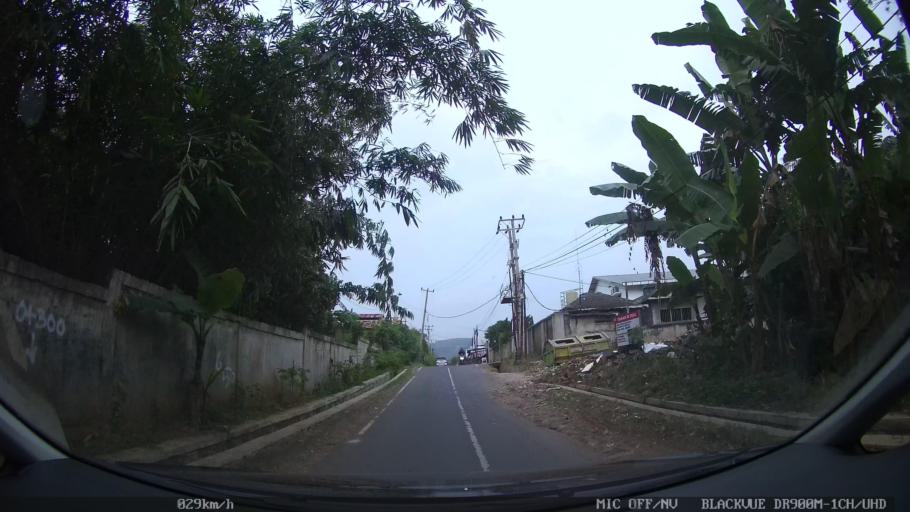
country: ID
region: Lampung
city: Bandarlampung
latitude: -5.4118
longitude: 105.2919
